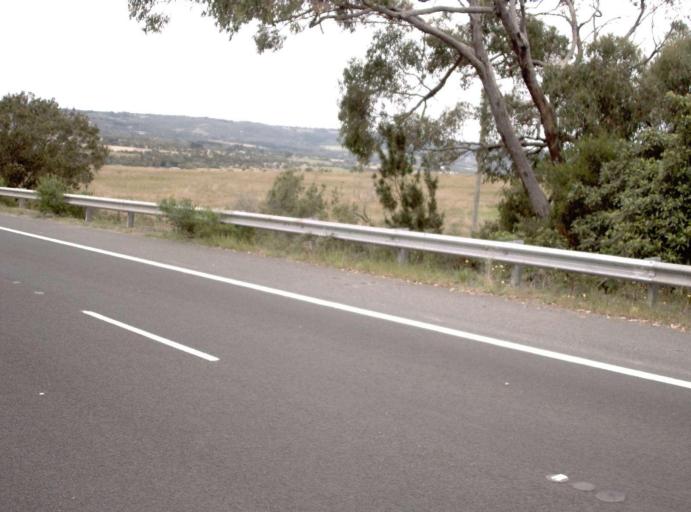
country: AU
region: Victoria
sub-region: Mornington Peninsula
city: Mount Martha
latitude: -38.2931
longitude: 145.0288
